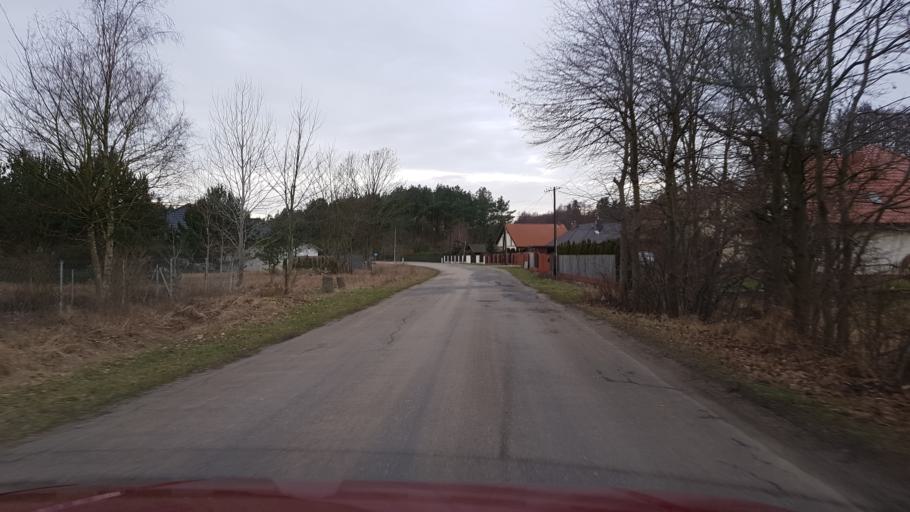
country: PL
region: West Pomeranian Voivodeship
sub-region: Powiat policki
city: Police
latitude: 53.5567
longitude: 14.4734
